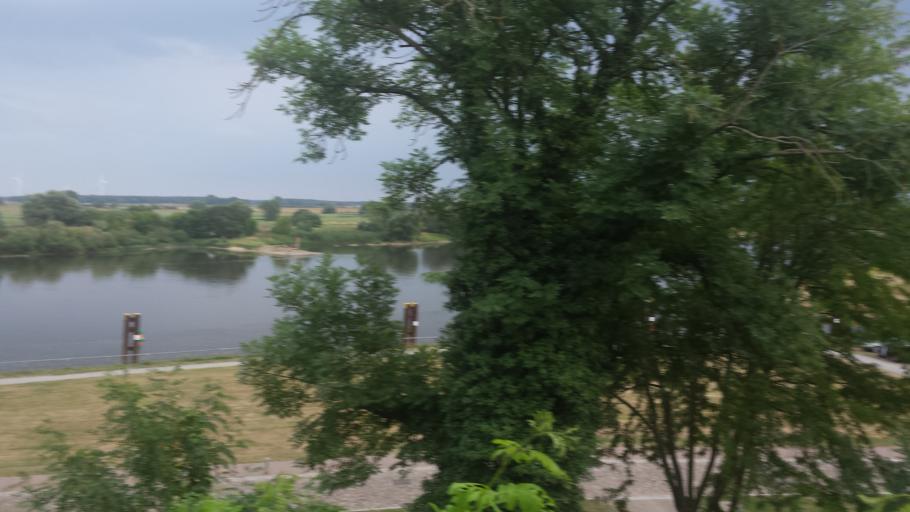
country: DE
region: Saxony-Anhalt
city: Tangermunde
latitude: 52.5430
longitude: 11.9785
